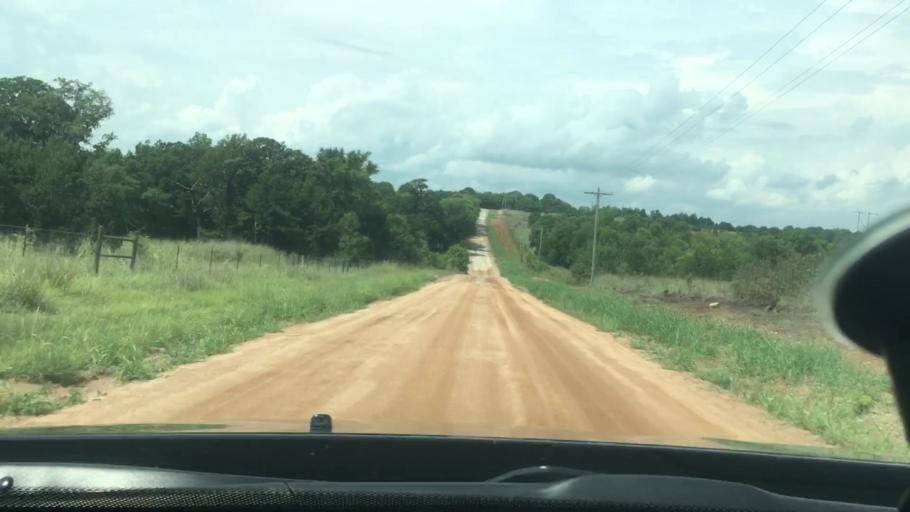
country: US
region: Oklahoma
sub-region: Carter County
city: Dickson
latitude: 34.2454
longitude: -96.9217
